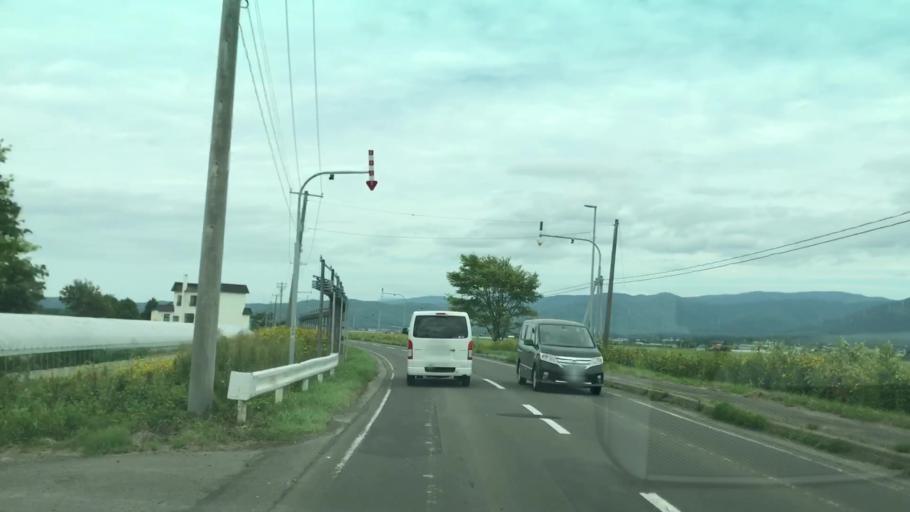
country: JP
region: Hokkaido
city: Iwanai
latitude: 43.0040
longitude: 140.5845
